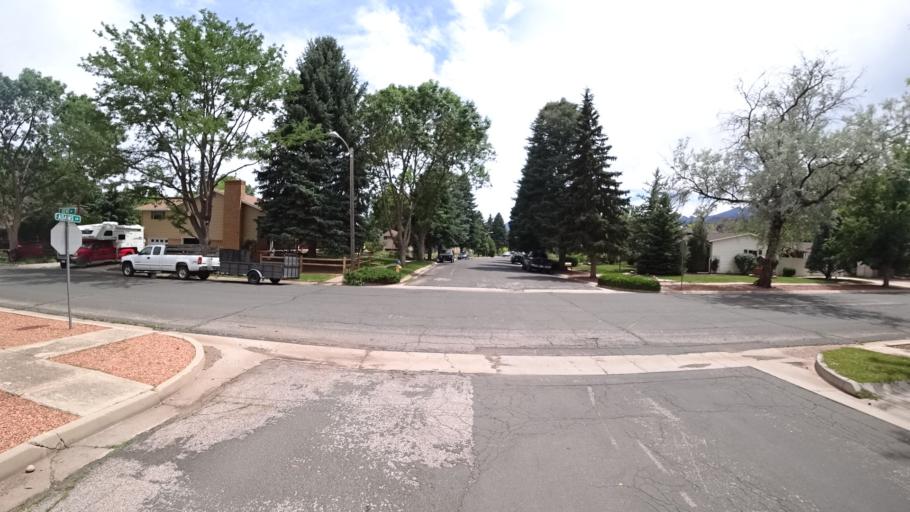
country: US
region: Colorado
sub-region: El Paso County
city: Manitou Springs
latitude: 38.8687
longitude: -104.8716
